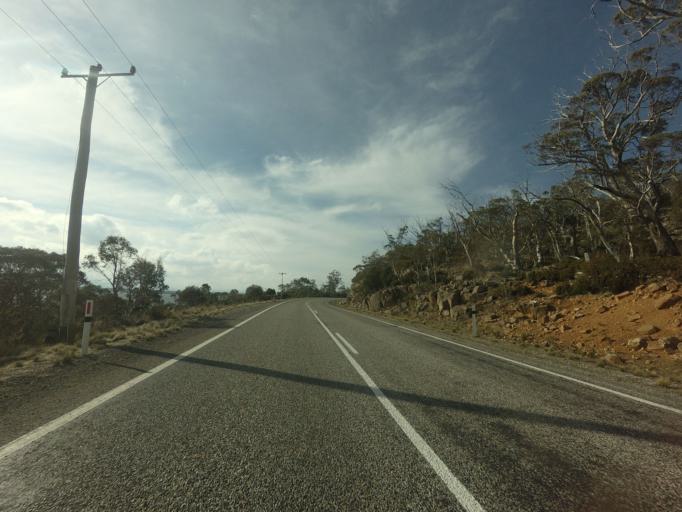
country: AU
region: Tasmania
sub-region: Meander Valley
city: Deloraine
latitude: -41.9872
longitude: 146.7107
